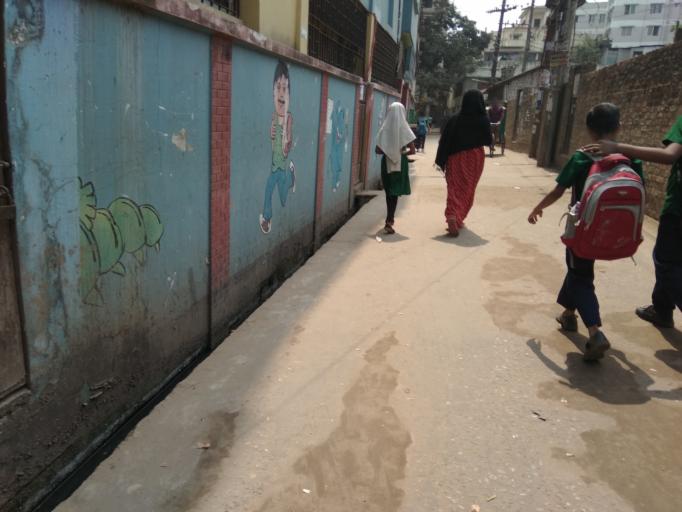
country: BD
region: Chittagong
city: Chittagong
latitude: 22.3704
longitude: 91.8354
